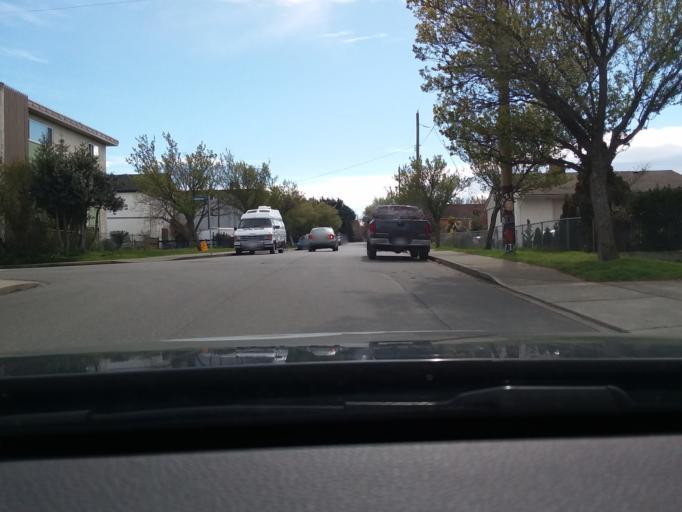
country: CA
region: British Columbia
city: Victoria
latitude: 48.4331
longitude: -123.3474
